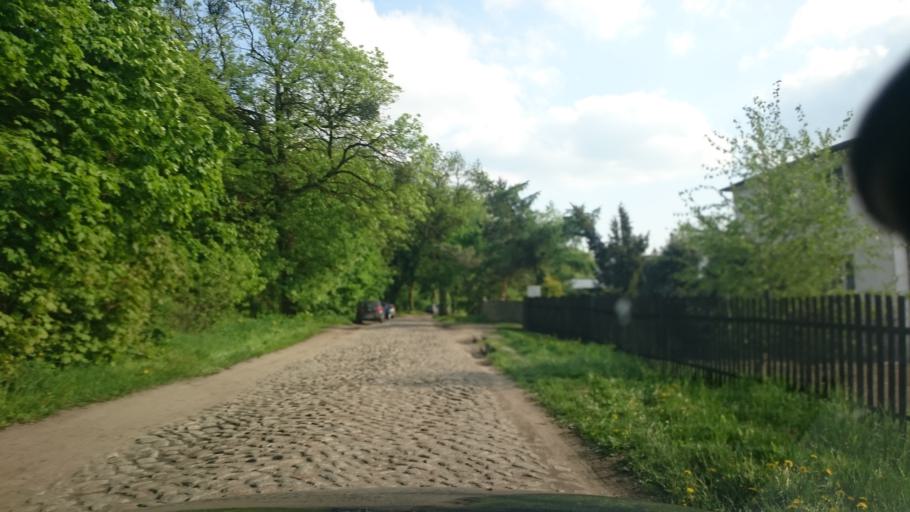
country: PL
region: Kujawsko-Pomorskie
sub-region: Grudziadz
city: Grudziadz
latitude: 53.4819
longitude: 18.8133
